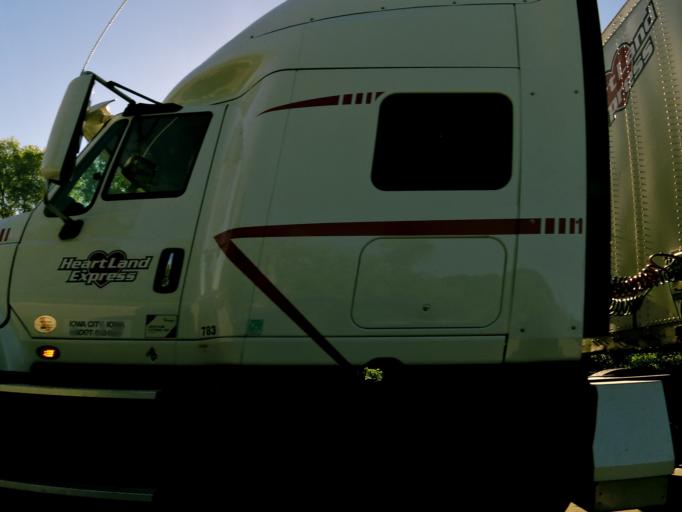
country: US
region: Minnesota
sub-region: Stearns County
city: Collegeville
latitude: 45.5770
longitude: -94.3571
